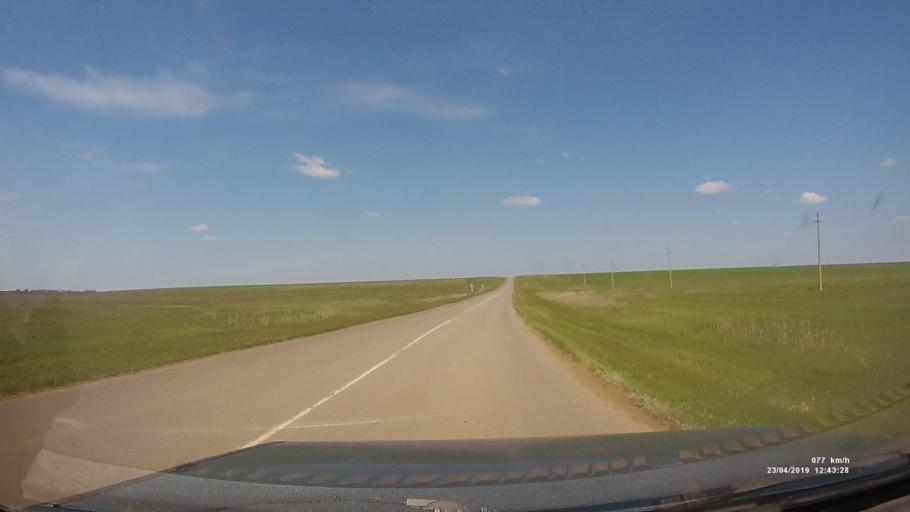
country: RU
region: Kalmykiya
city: Yashalta
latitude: 46.4644
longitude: 42.6505
